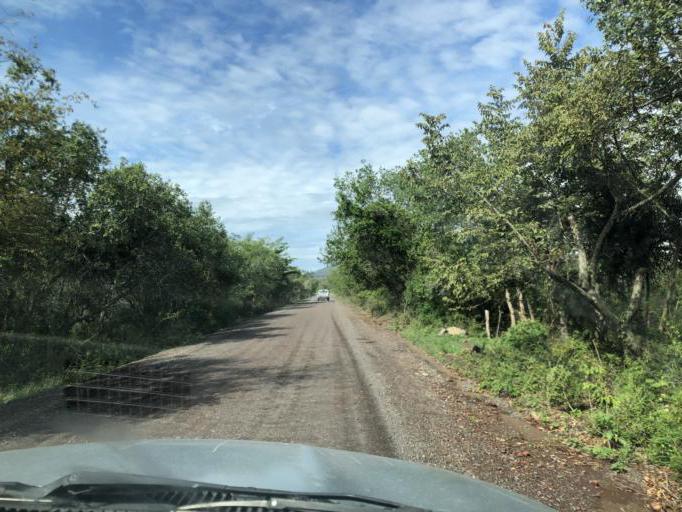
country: MX
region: Veracruz
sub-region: Alto Lucero de Gutierrez Barrios
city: Palma Sola
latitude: 19.7930
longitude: -96.5498
